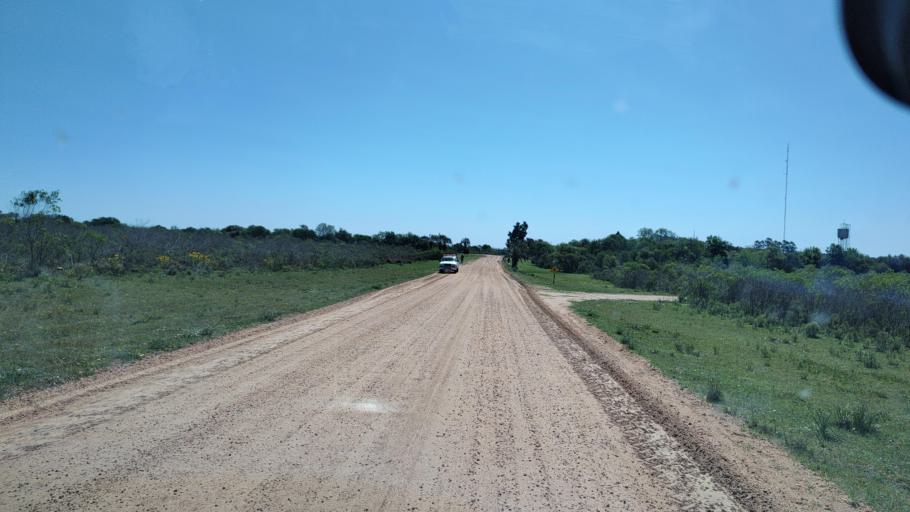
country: AR
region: Entre Rios
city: Ubajay
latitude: -31.8657
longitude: -58.2570
